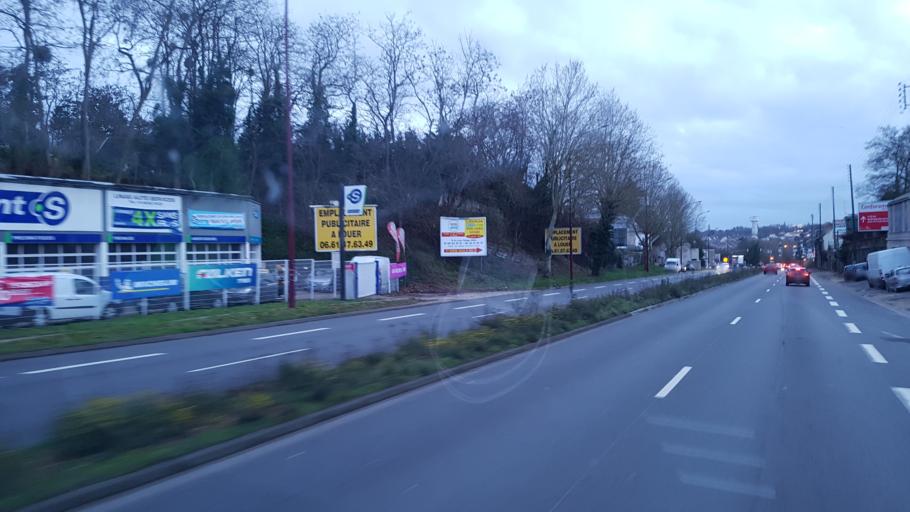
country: FR
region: Ile-de-France
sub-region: Departement de l'Essonne
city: Montlhery
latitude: 48.6374
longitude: 2.2671
